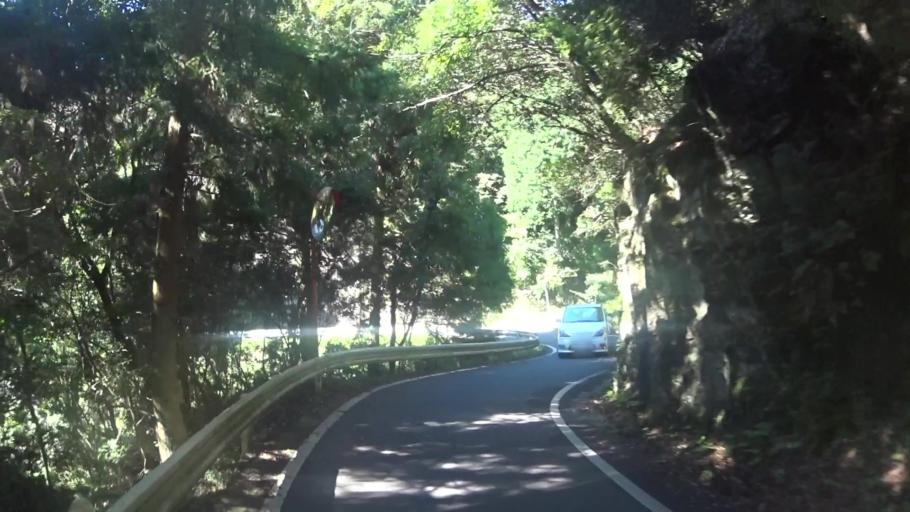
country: JP
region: Kyoto
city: Uji
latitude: 34.8205
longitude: 135.8889
